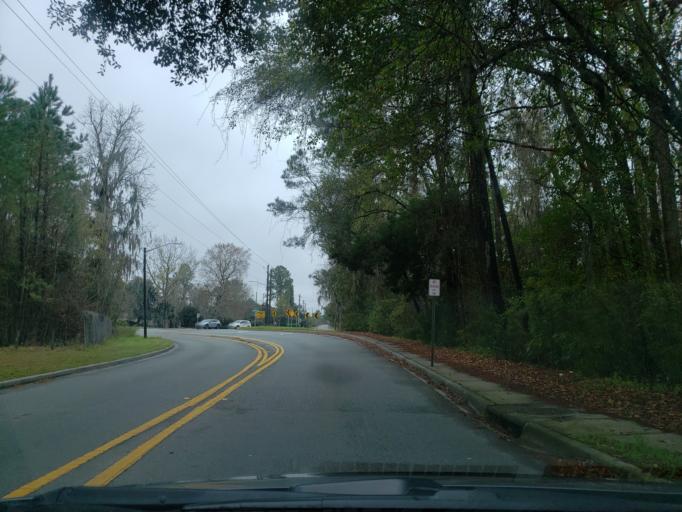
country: US
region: Georgia
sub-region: Chatham County
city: Georgetown
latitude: 31.9782
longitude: -81.1702
